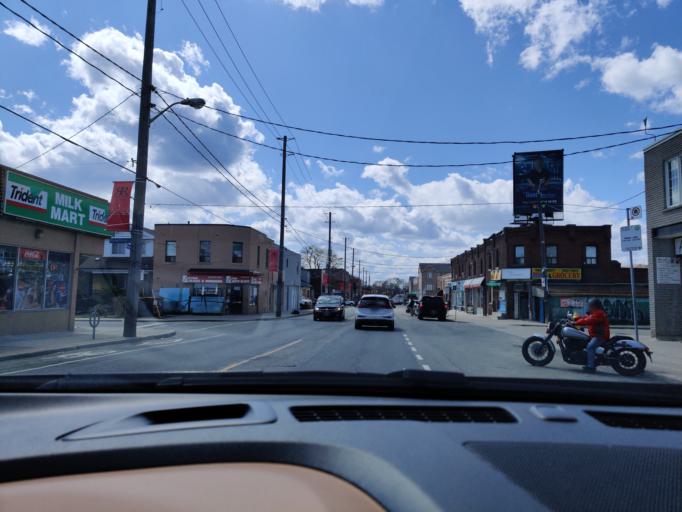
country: CA
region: Ontario
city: Toronto
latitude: 43.6827
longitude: -79.4640
